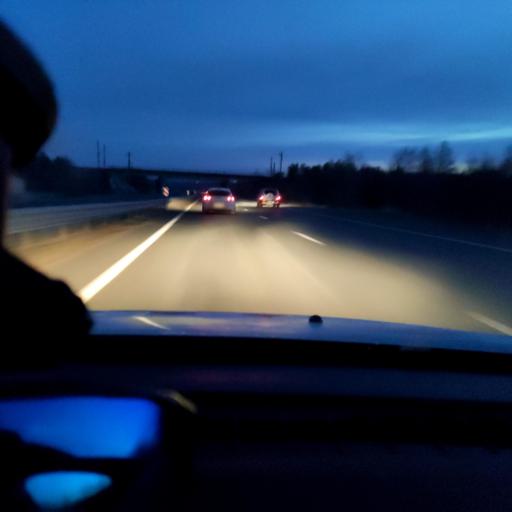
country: RU
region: Samara
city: Novokuybyshevsk
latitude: 53.0185
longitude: 49.9827
